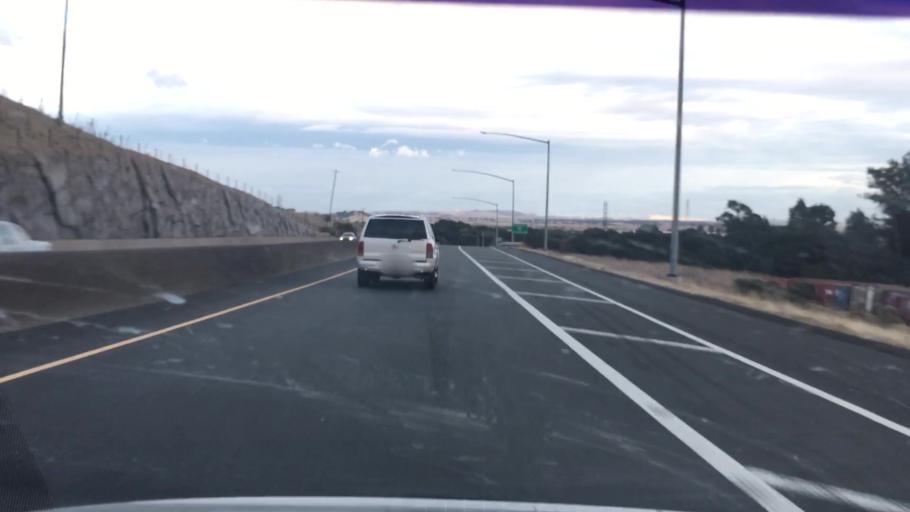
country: US
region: California
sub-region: Solano County
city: Green Valley
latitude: 38.2076
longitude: -122.1621
